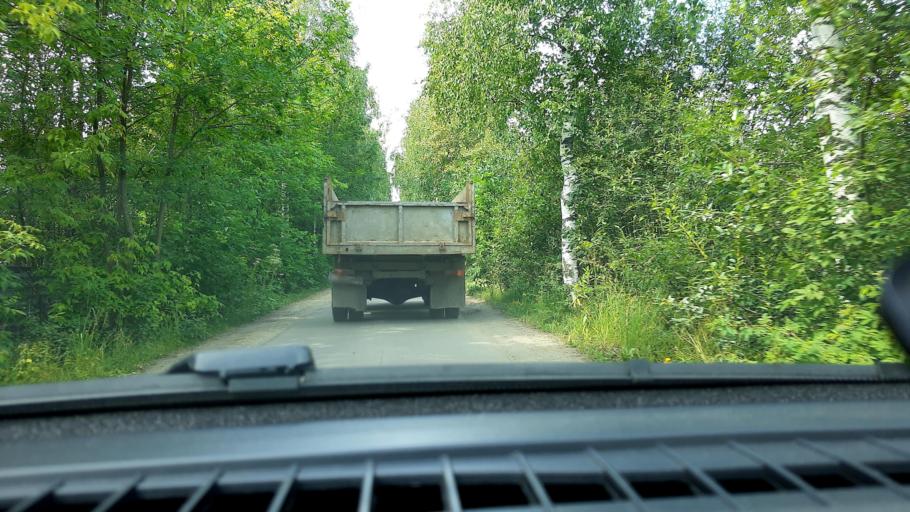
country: RU
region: Nizjnij Novgorod
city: Gorbatovka
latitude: 56.2490
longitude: 43.8194
